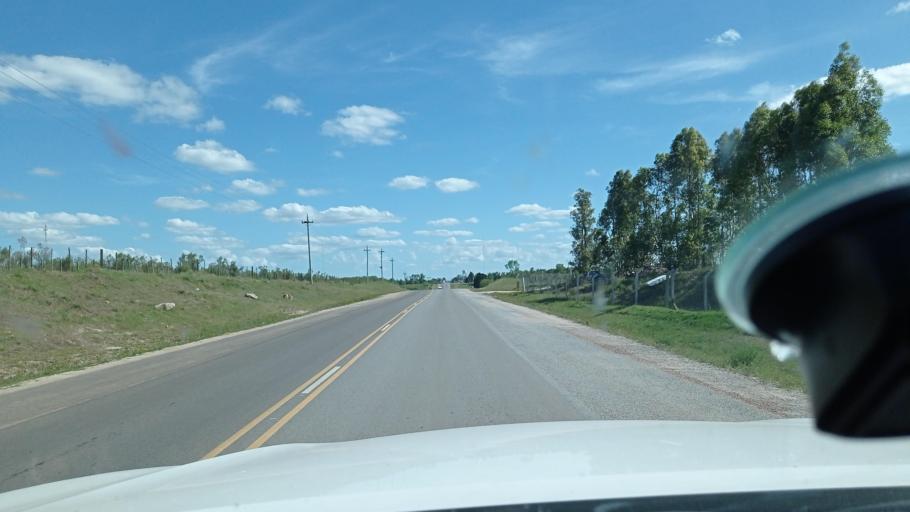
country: UY
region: Florida
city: Florida
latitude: -34.0776
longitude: -56.2346
